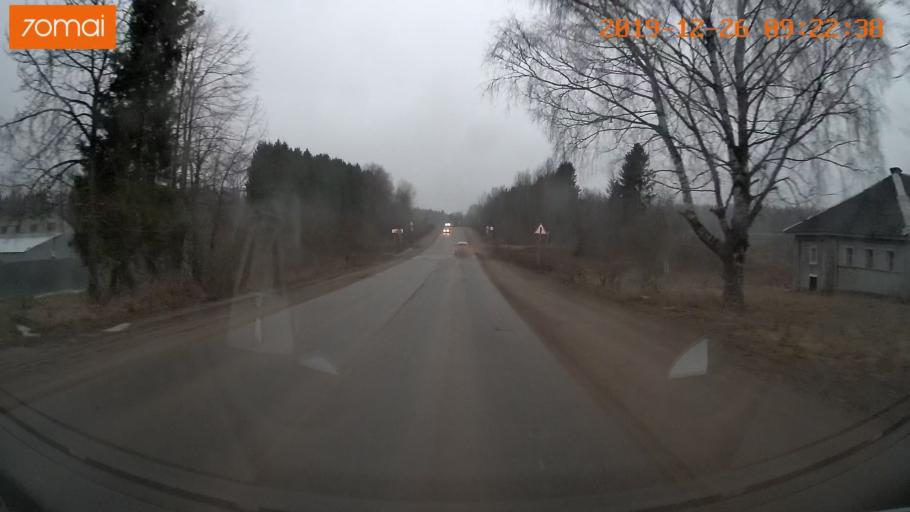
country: RU
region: Vologda
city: Gryazovets
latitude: 58.9827
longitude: 40.2142
